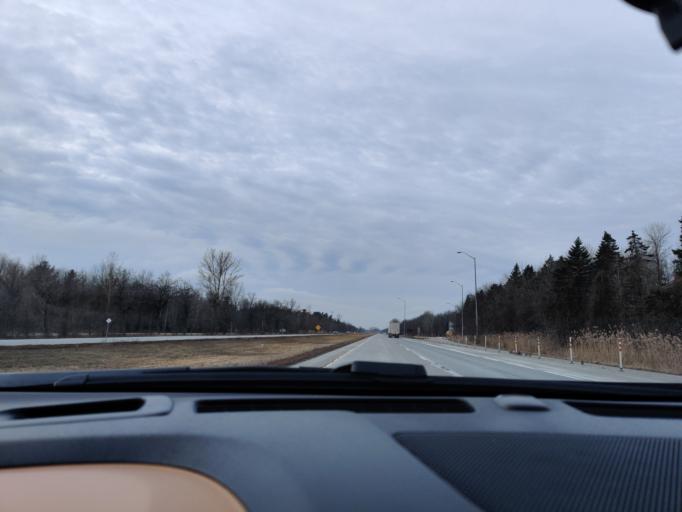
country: CA
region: Quebec
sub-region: Monteregie
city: Les Coteaux
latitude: 45.1569
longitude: -74.4590
